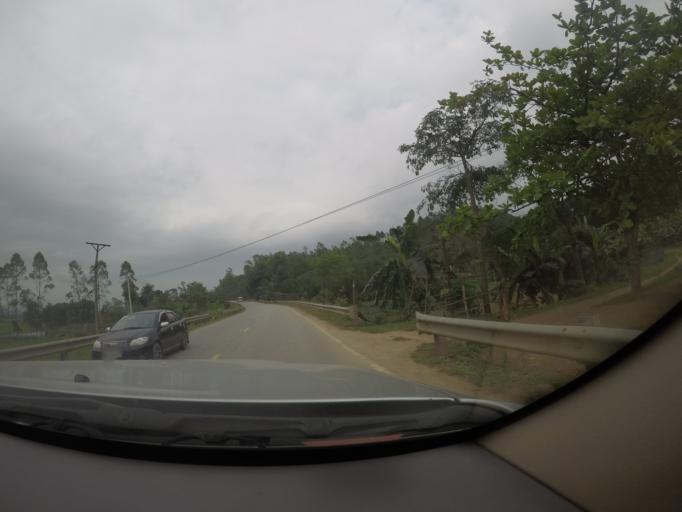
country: VN
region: Quang Binh
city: Ba Don
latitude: 17.6083
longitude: 106.3454
